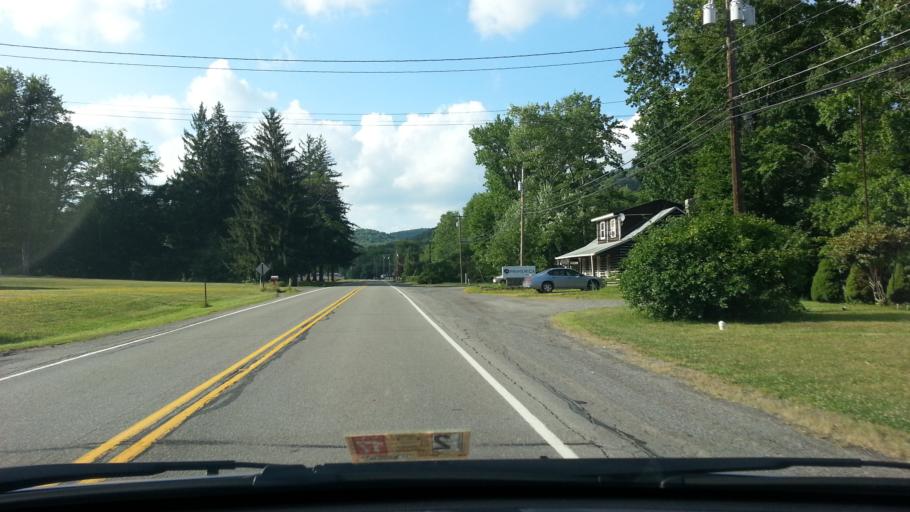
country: US
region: Pennsylvania
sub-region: Elk County
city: Saint Marys
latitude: 41.2838
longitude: -78.5010
